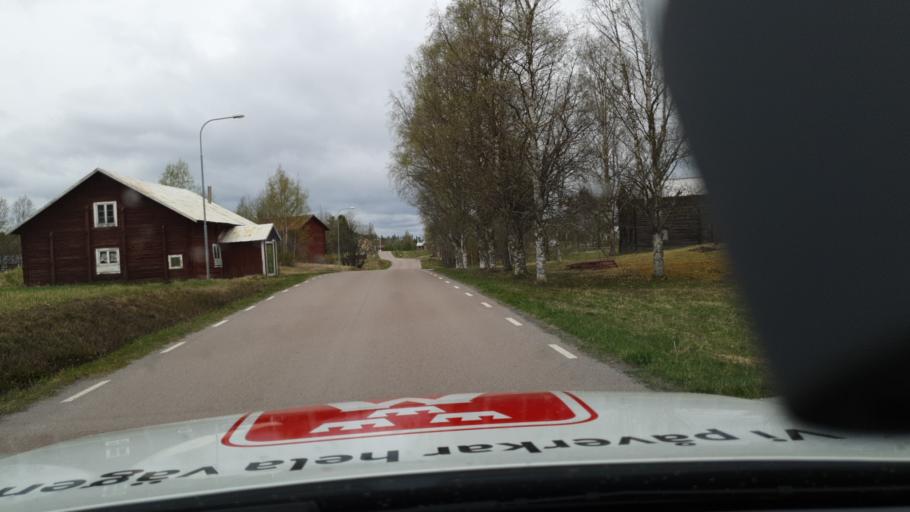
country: SE
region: Jaemtland
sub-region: OEstersunds Kommun
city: Lit
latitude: 63.2998
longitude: 14.9646
